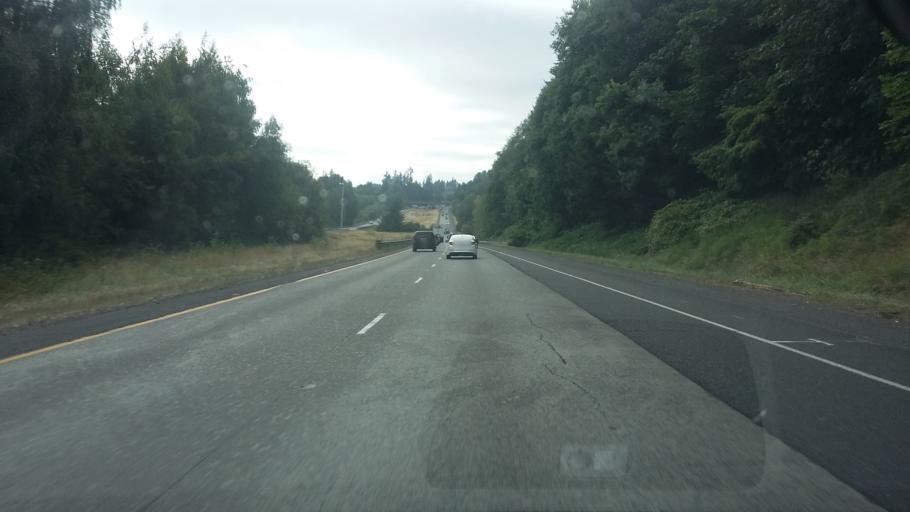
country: US
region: Washington
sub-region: Clark County
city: Salmon Creek
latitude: 45.7134
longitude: -122.6430
